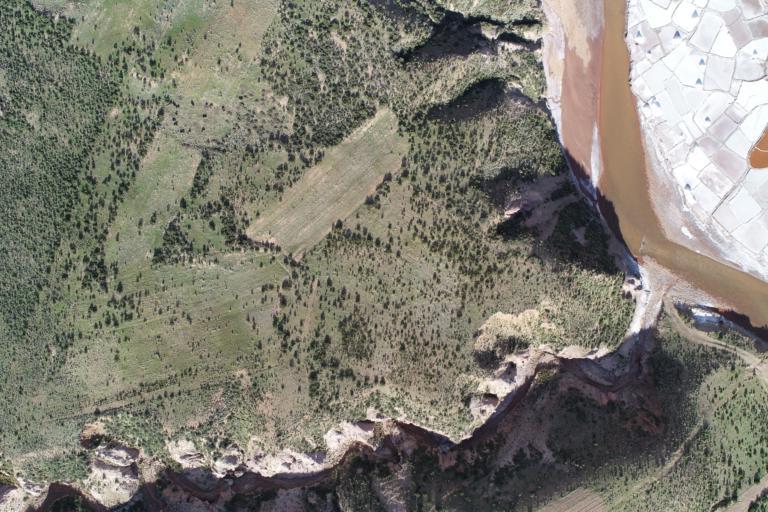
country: BO
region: La Paz
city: Patacamaya
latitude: -17.2989
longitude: -68.4884
